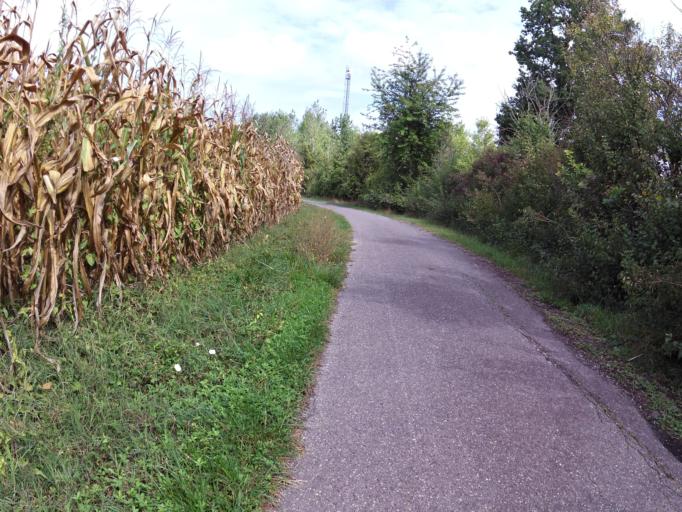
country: FR
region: Alsace
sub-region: Departement du Haut-Rhin
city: Biesheim
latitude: 48.0437
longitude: 7.5537
